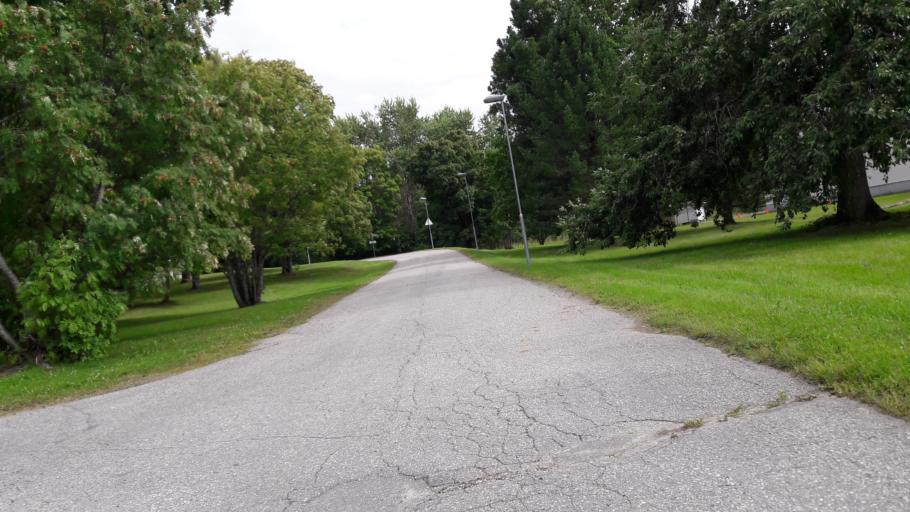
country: FI
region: North Karelia
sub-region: Joensuu
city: Joensuu
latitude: 62.5749
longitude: 29.7972
